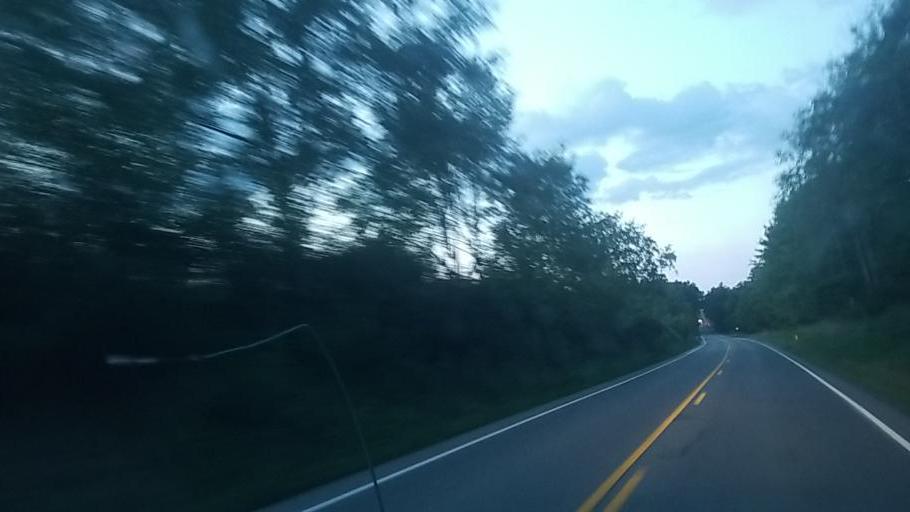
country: US
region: Pennsylvania
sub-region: Clarion County
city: Knox
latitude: 41.1980
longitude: -79.5446
